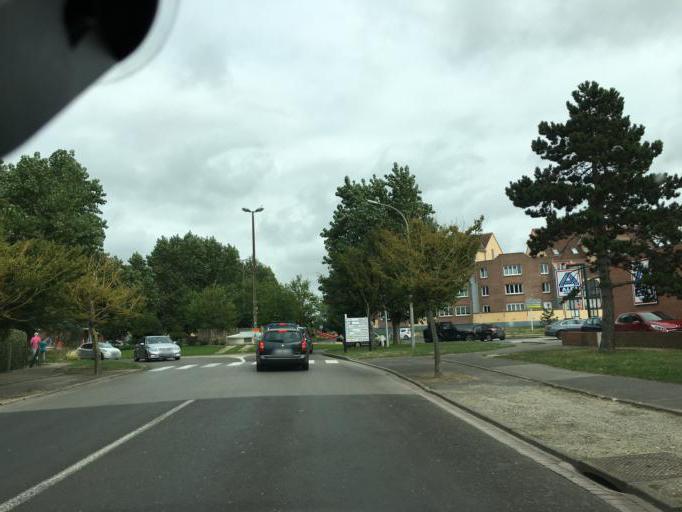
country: FR
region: Nord-Pas-de-Calais
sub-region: Departement du Pas-de-Calais
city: Berck-Plage
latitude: 50.4035
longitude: 1.5781
